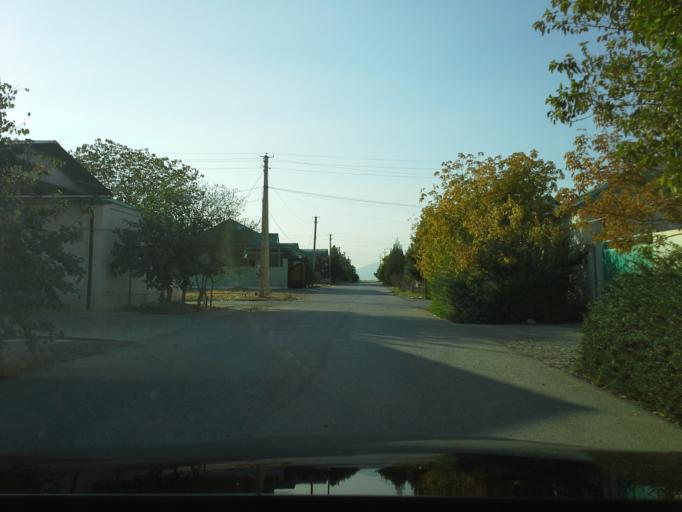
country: TM
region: Ahal
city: Abadan
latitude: 38.0434
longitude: 58.1663
